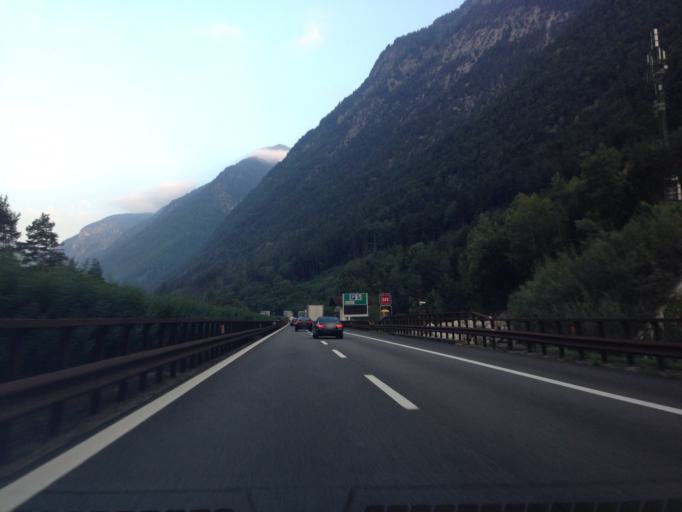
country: IT
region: Trentino-Alto Adige
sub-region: Bolzano
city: Fortezza
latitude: 46.7947
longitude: 11.6079
